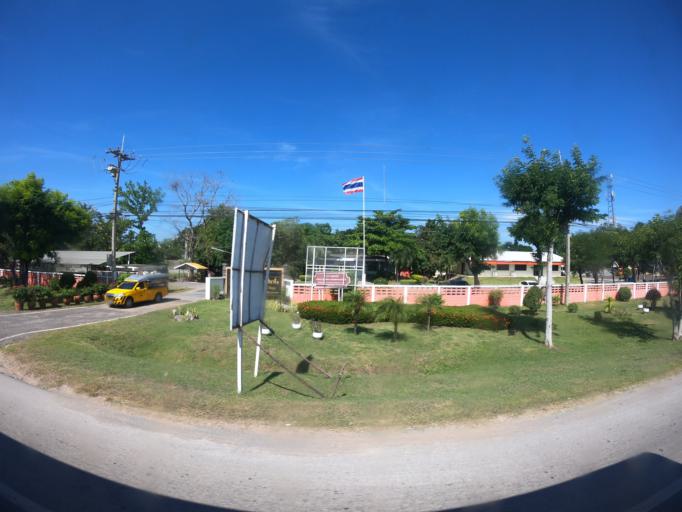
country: TH
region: Nakhon Ratchasima
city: Nakhon Ratchasima
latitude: 15.0490
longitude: 102.1545
